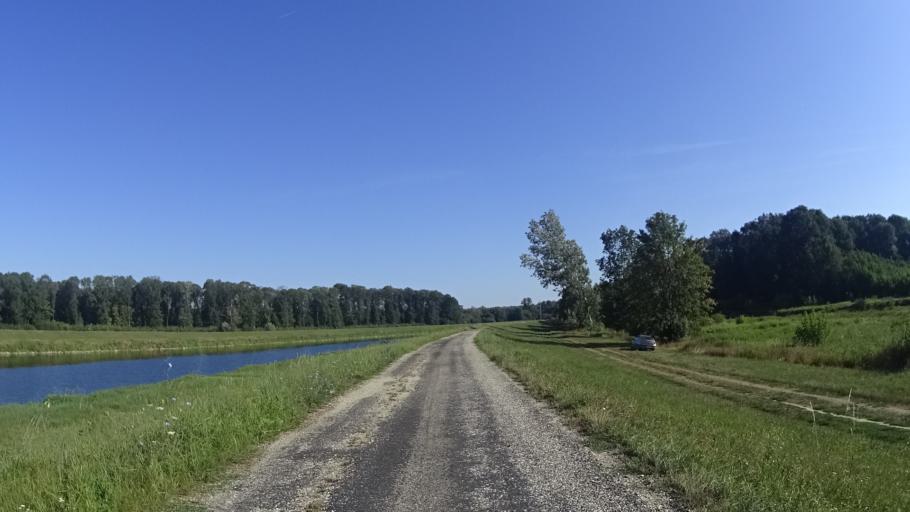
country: CZ
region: South Moravian
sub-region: Okres Breclav
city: Lanzhot
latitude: 48.7056
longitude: 16.9975
